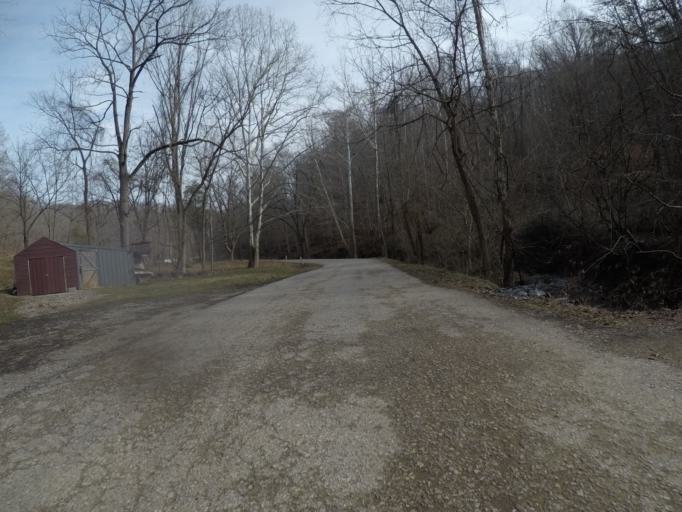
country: US
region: West Virginia
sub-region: Wayne County
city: Lavalette
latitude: 38.3606
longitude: -82.3981
